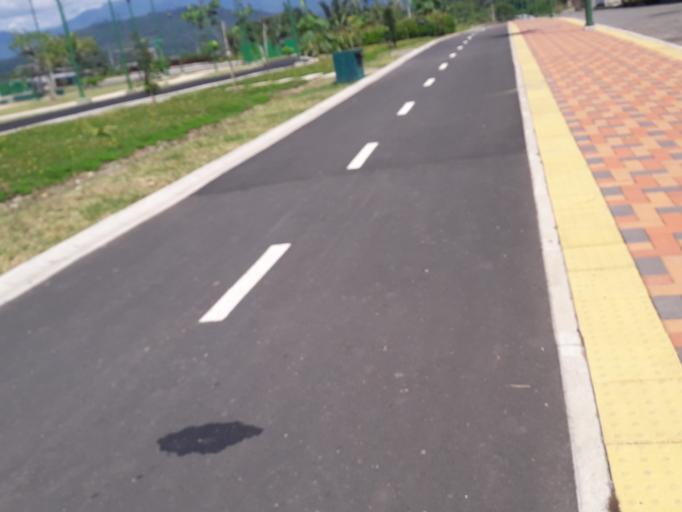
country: EC
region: Napo
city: Tena
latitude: -0.9855
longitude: -77.8226
